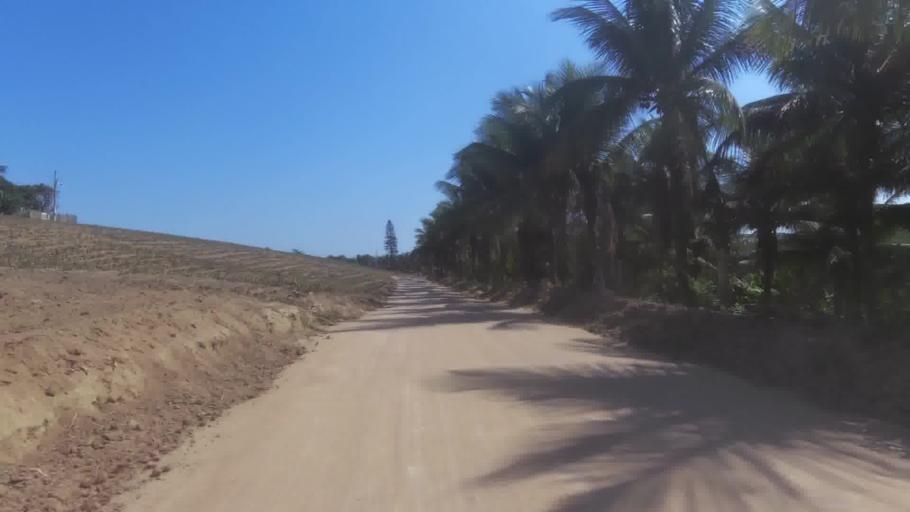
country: BR
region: Espirito Santo
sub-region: Marataizes
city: Marataizes
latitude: -21.1062
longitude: -40.8566
